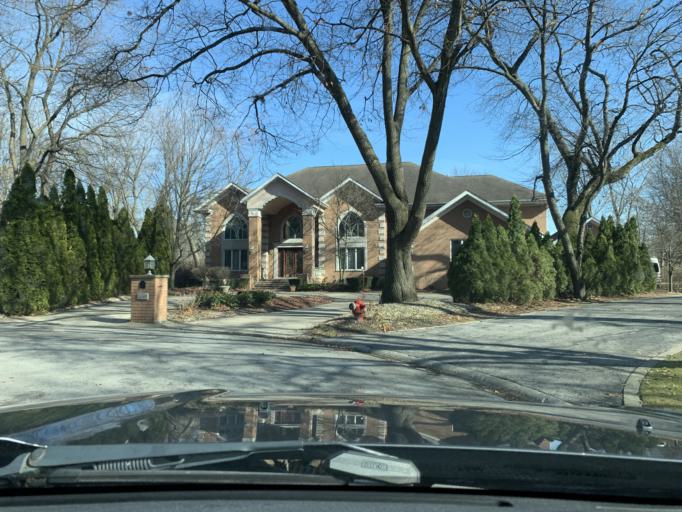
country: US
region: Indiana
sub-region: Lake County
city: Dyer
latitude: 41.5158
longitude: -87.4829
